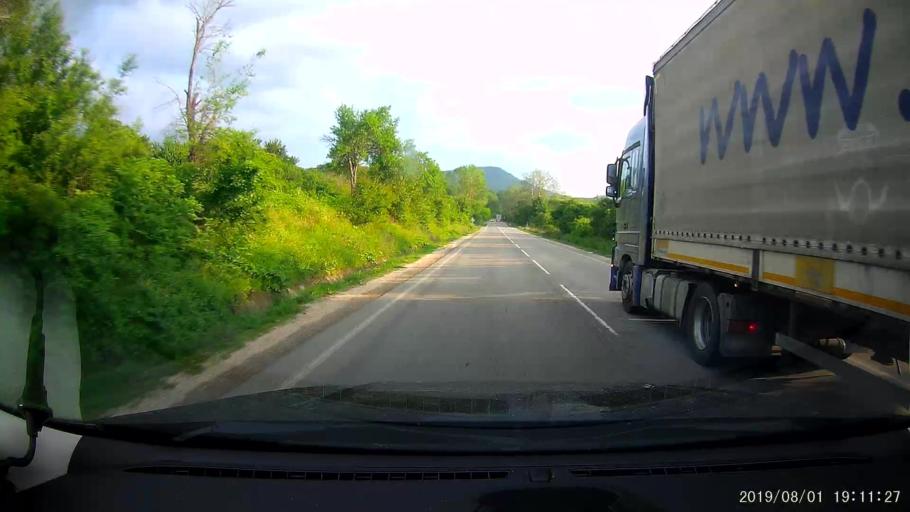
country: BG
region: Shumen
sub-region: Obshtina Smyadovo
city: Smyadovo
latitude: 42.9745
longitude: 26.9610
